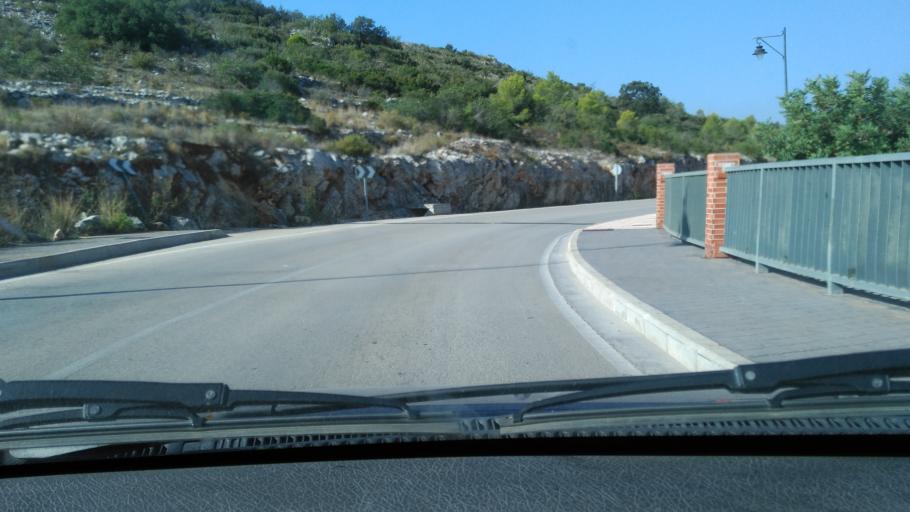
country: ES
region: Valencia
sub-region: Provincia de Alicante
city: Gata de Gorgos
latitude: 38.7702
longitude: 0.0905
